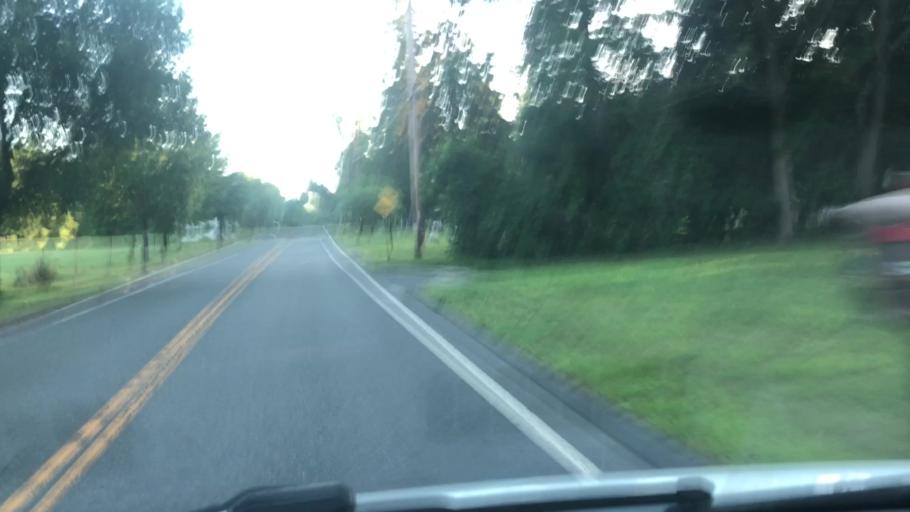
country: US
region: Massachusetts
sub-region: Hampshire County
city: Westhampton
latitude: 42.3014
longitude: -72.7166
